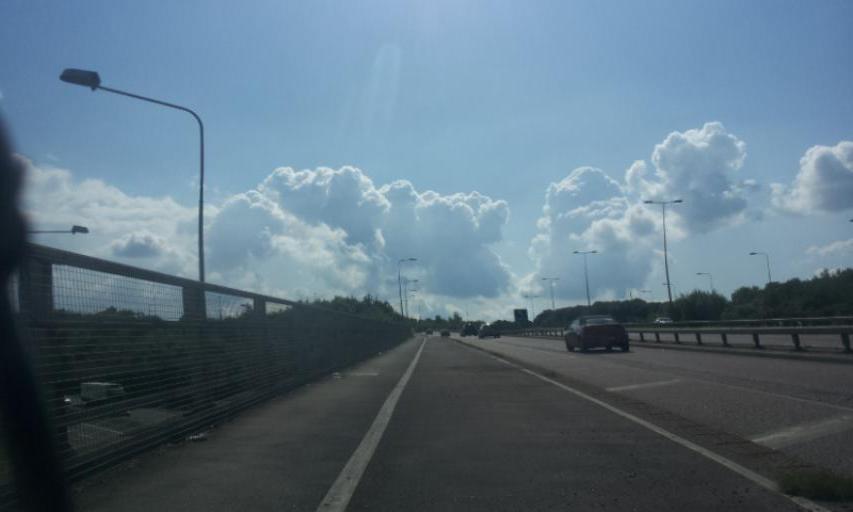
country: GB
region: England
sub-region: Kent
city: Aylesford
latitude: 51.3397
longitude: 0.5057
